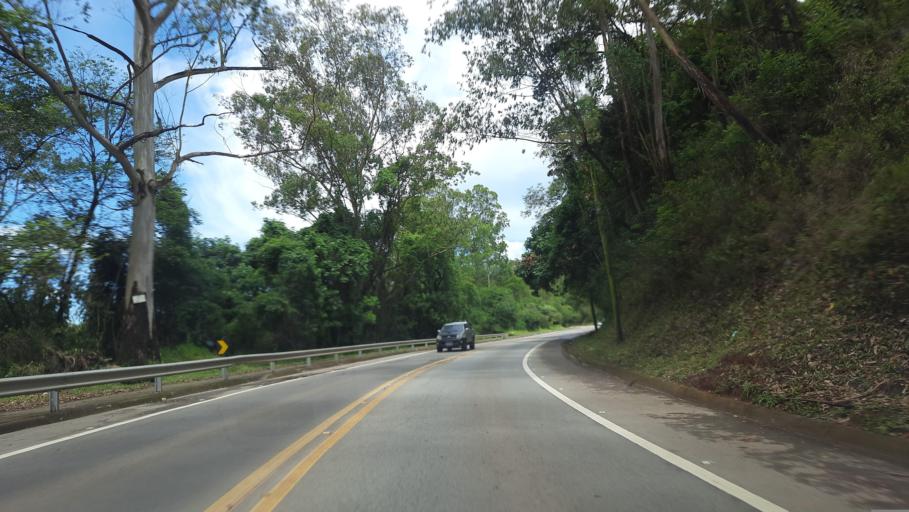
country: BR
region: Sao Paulo
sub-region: Franco Da Rocha
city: Franco da Rocha
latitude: -23.3313
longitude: -46.6940
